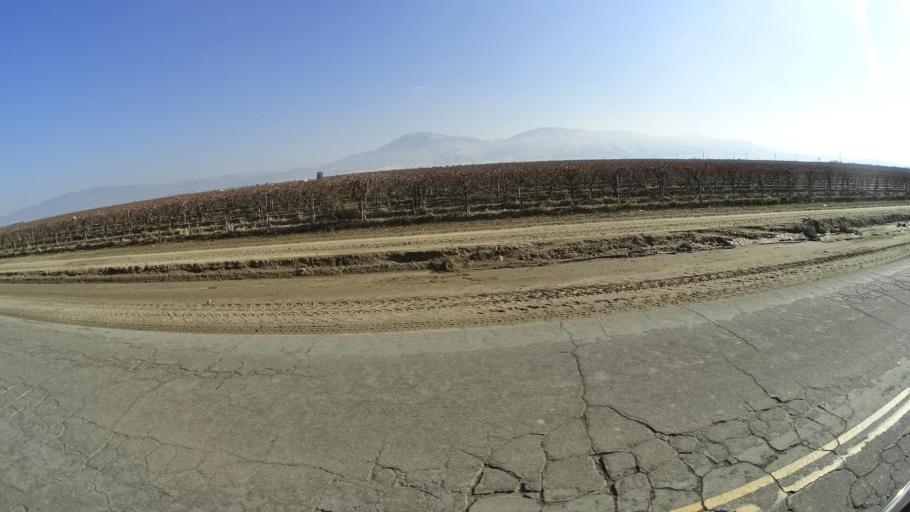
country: US
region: California
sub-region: Kern County
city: Arvin
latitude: 35.1969
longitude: -118.8782
